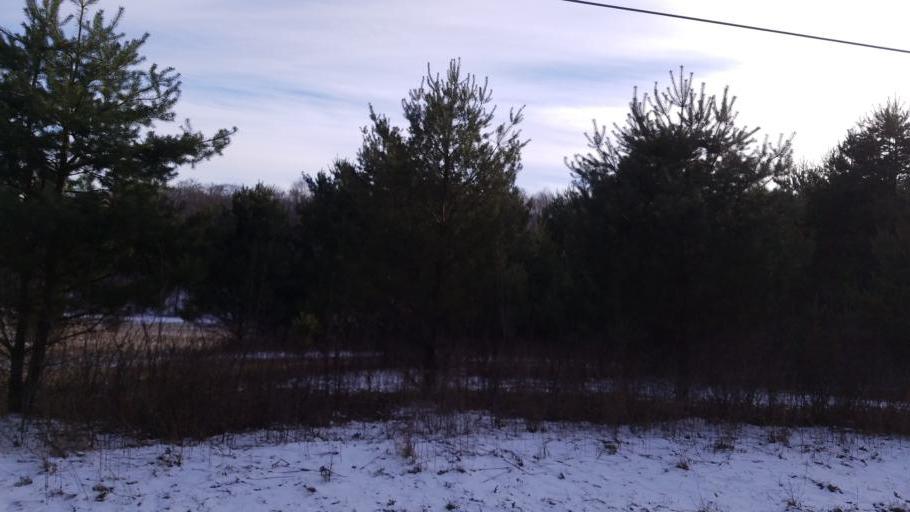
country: US
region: New York
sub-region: Allegany County
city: Wellsville
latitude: 42.1832
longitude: -77.8846
